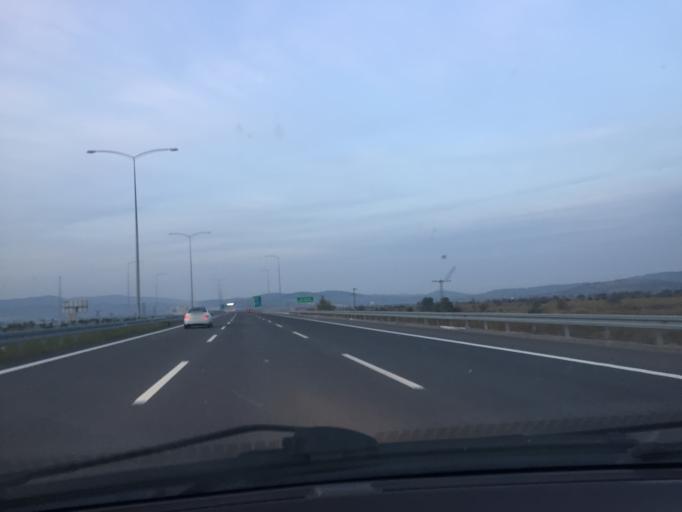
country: TR
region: Manisa
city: Halitpasa
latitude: 38.7562
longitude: 27.6603
